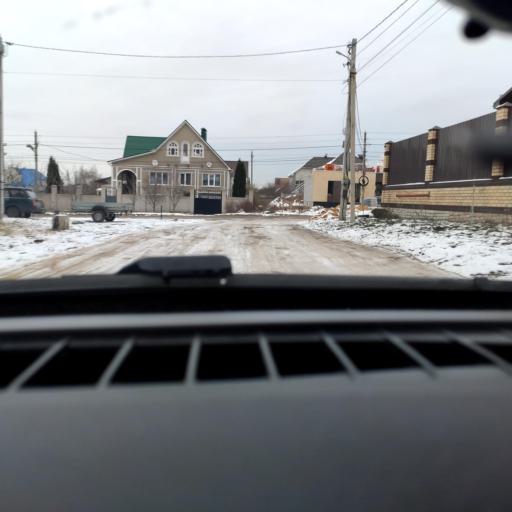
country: RU
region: Voronezj
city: Podgornoye
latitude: 51.7238
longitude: 39.1394
